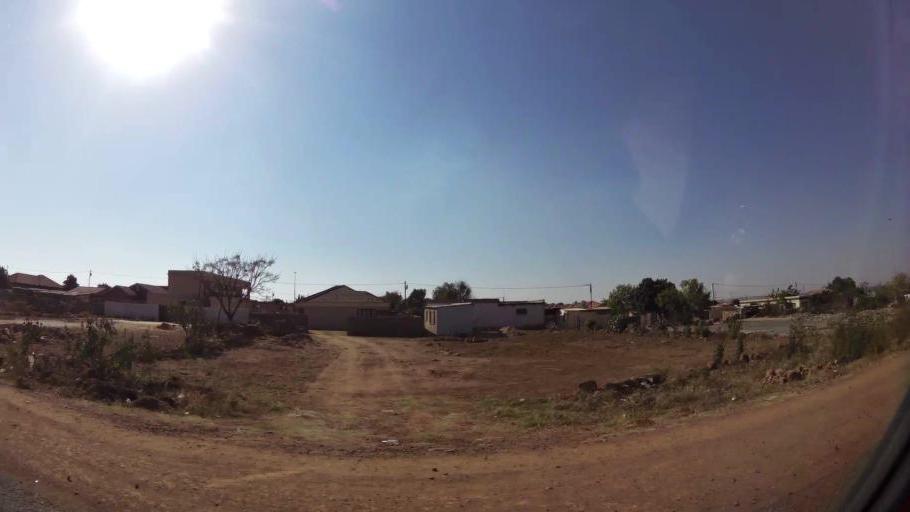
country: ZA
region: Gauteng
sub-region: City of Tshwane Metropolitan Municipality
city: Mabopane
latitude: -25.5546
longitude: 28.0985
